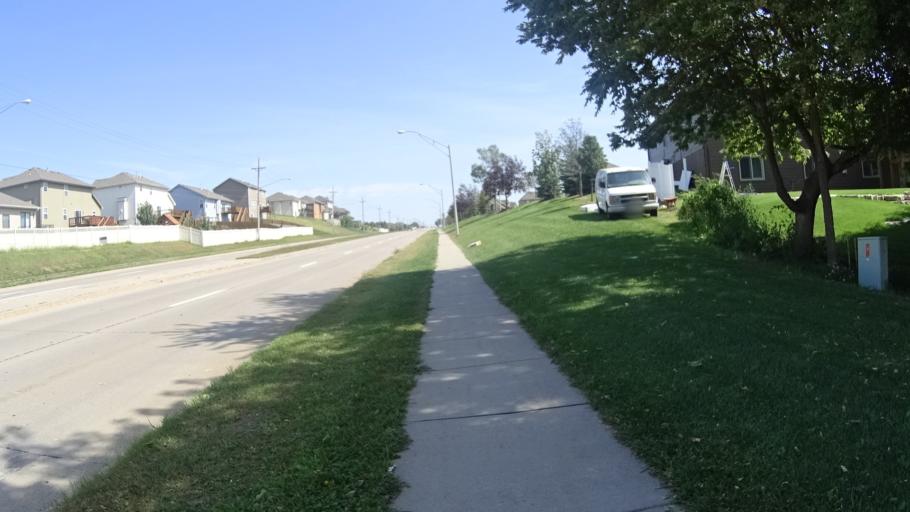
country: US
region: Nebraska
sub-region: Sarpy County
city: Papillion
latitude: 41.1762
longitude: -96.0771
